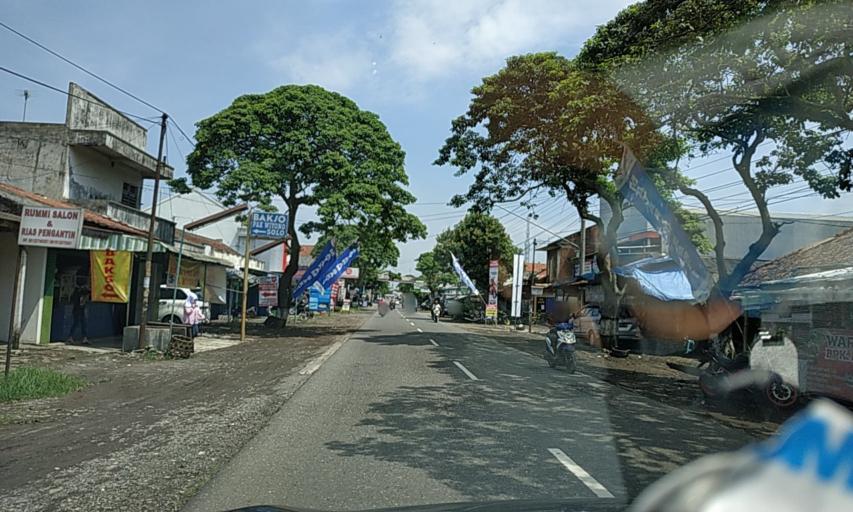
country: ID
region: Central Java
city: Gendiwu
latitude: -7.4862
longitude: 108.8099
